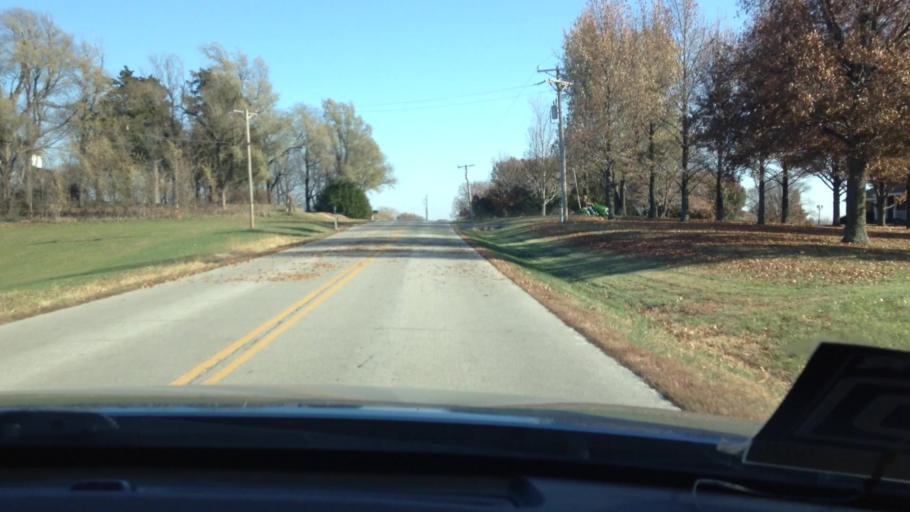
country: US
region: Missouri
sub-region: Platte County
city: Weston
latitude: 39.4277
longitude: -94.8622
